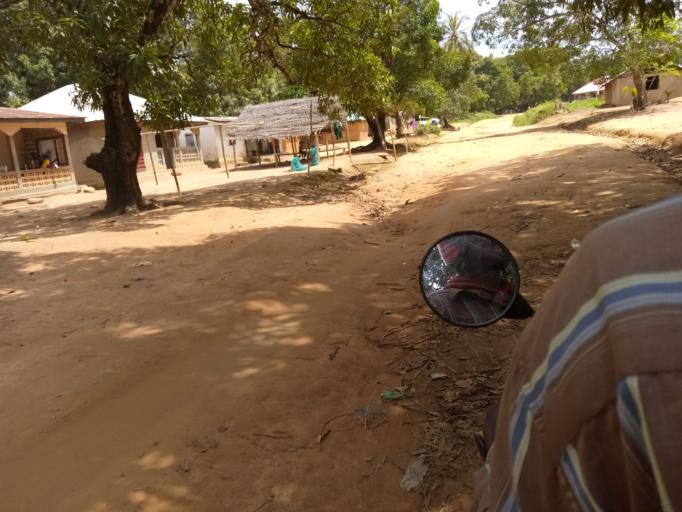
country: SL
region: Western Area
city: Waterloo
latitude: 8.4108
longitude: -13.0040
